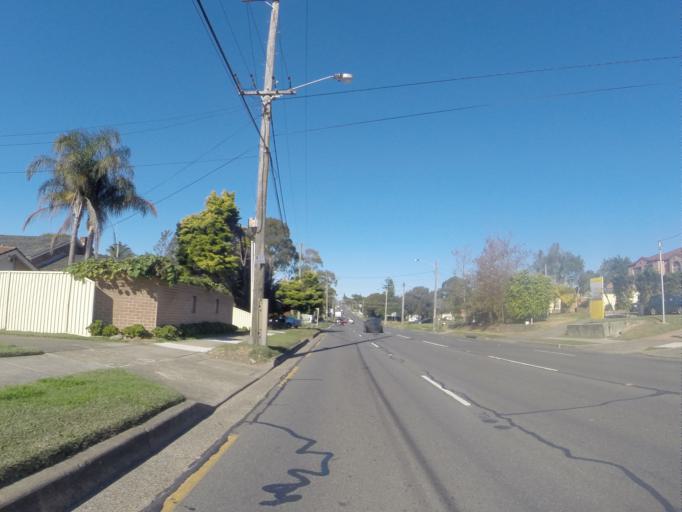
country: AU
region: New South Wales
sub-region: Hurstville
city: Penshurst
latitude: -33.9575
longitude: 151.0876
